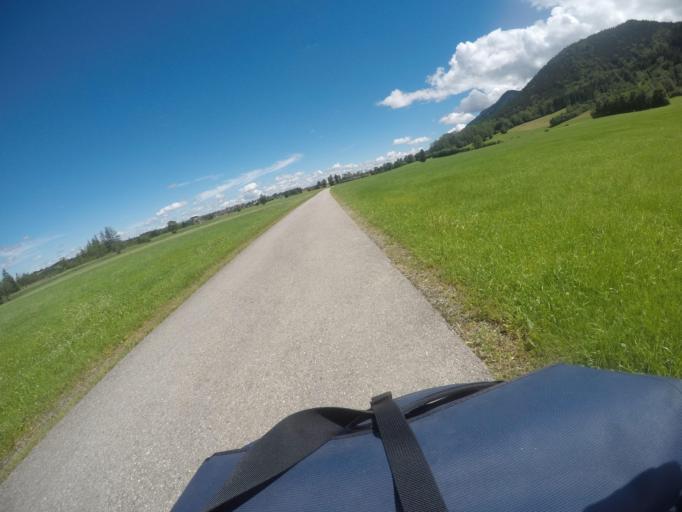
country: DE
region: Bavaria
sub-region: Swabia
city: Halblech
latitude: 47.6048
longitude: 10.7935
